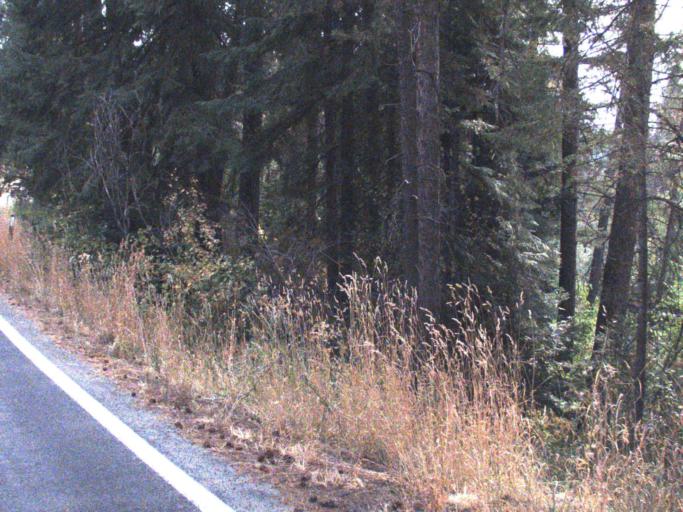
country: US
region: Washington
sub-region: Spokane County
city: Trentwood
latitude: 47.8339
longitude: -117.1995
